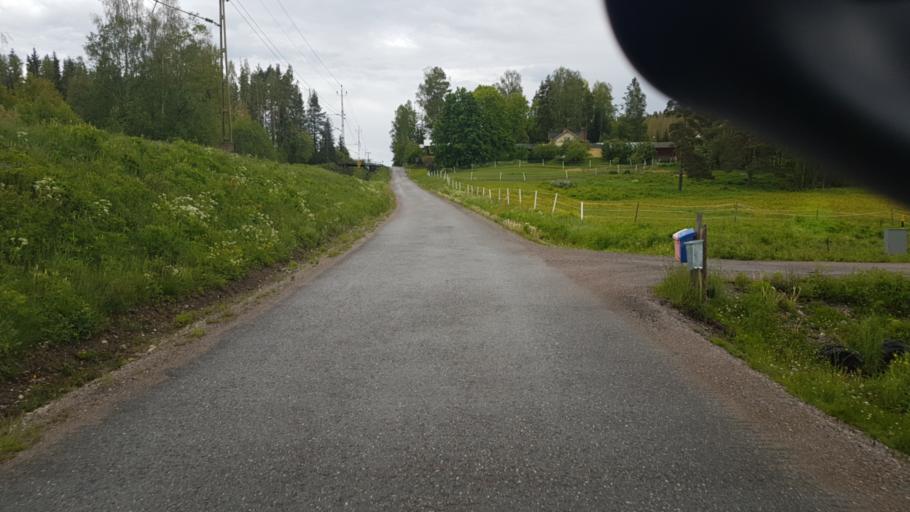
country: SE
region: Vaermland
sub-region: Eda Kommun
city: Amotfors
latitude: 59.8219
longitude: 12.3644
